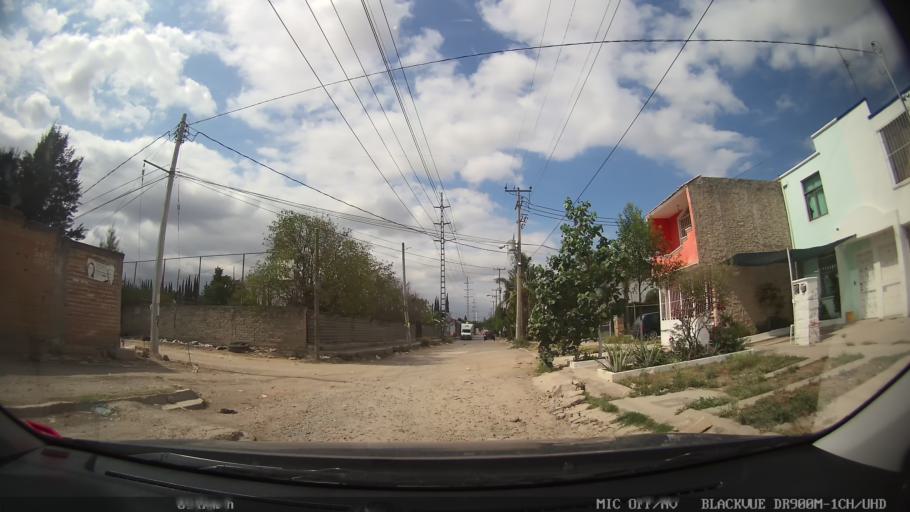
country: MX
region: Jalisco
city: Tonala
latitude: 20.6623
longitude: -103.2475
